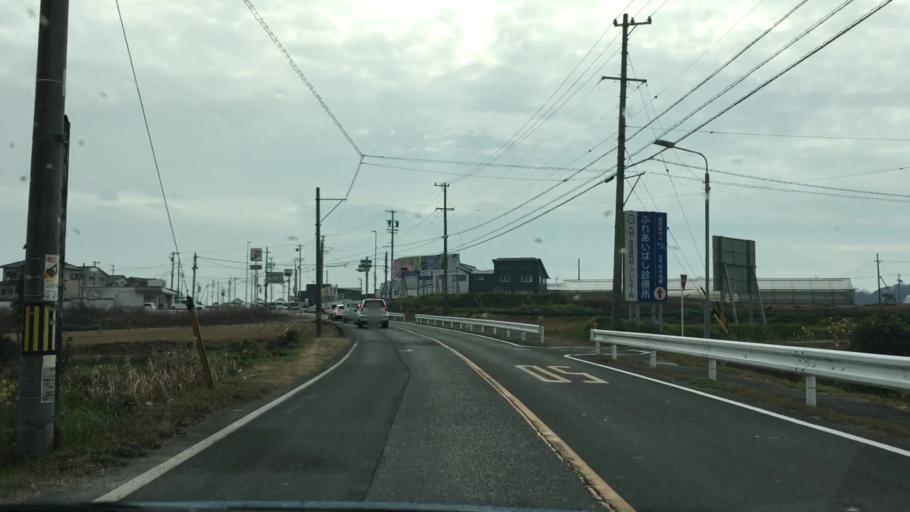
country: JP
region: Aichi
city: Tahara
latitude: 34.6941
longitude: 137.2775
